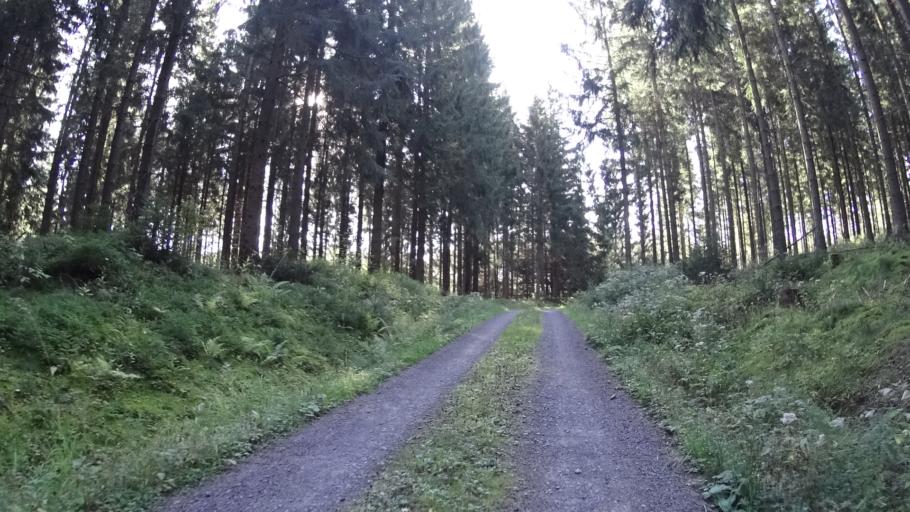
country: DE
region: Thuringia
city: Neuhaus
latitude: 50.6393
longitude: 10.9285
